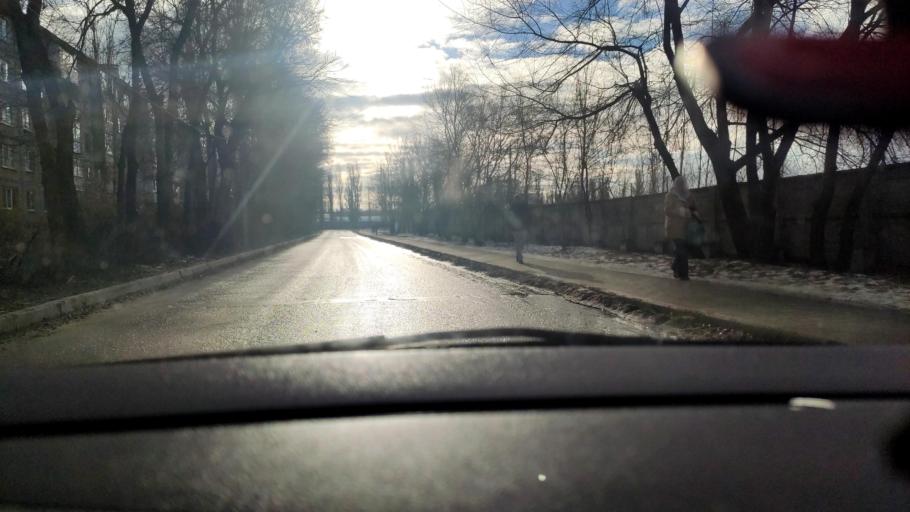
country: RU
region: Voronezj
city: Pridonskoy
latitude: 51.6241
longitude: 39.0686
